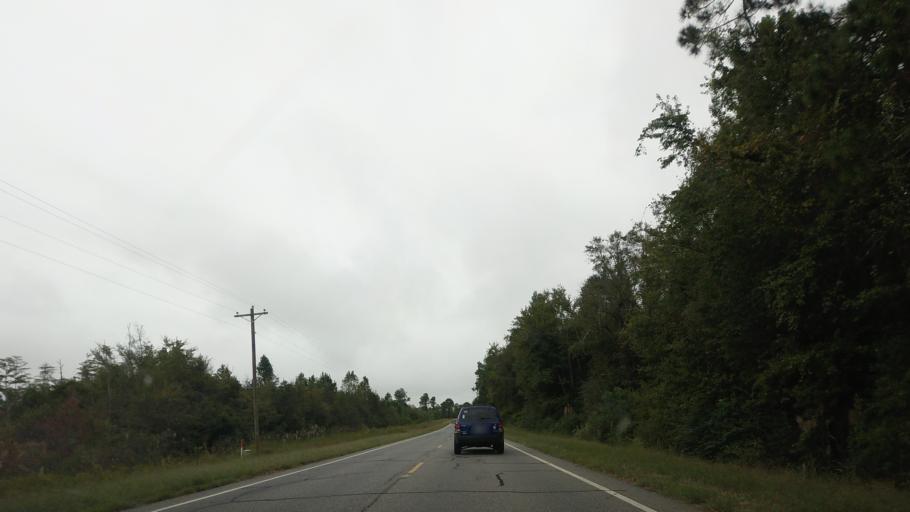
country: US
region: Georgia
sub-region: Irwin County
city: Ocilla
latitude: 31.5461
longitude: -83.2539
